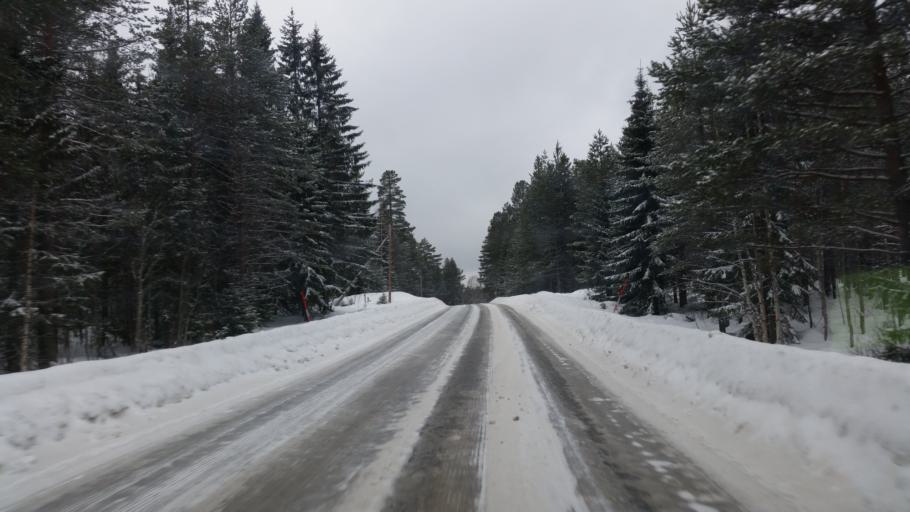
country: SE
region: Jaemtland
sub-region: Bergs Kommun
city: Hoverberg
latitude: 62.4645
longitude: 14.4903
